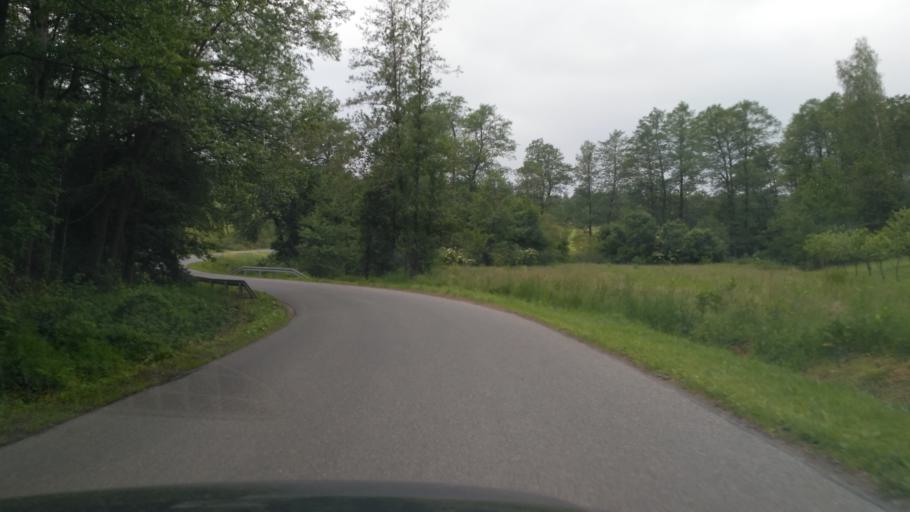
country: PL
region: Subcarpathian Voivodeship
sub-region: Powiat ropczycko-sedziszowski
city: Zagorzyce
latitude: 49.9969
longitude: 21.6902
